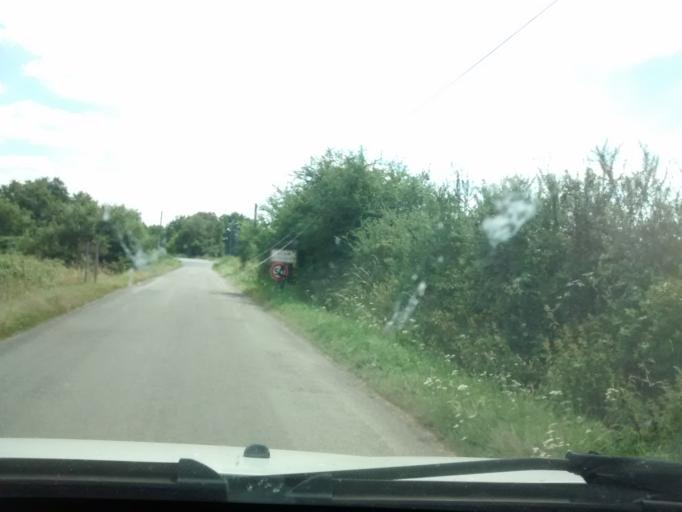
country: FR
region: Brittany
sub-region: Departement d'Ille-et-Vilaine
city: Vezin-le-Coquet
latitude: 48.1194
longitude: -1.7418
